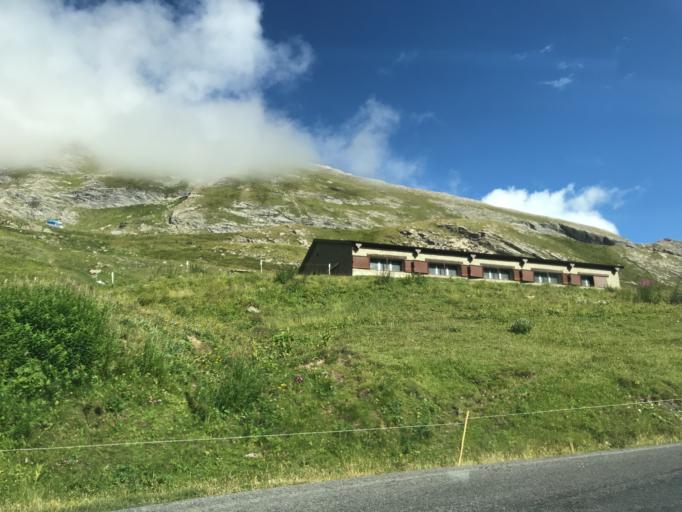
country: IT
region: Piedmont
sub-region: Provincia di Cuneo
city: Pontechianale
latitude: 44.6721
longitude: 6.9867
